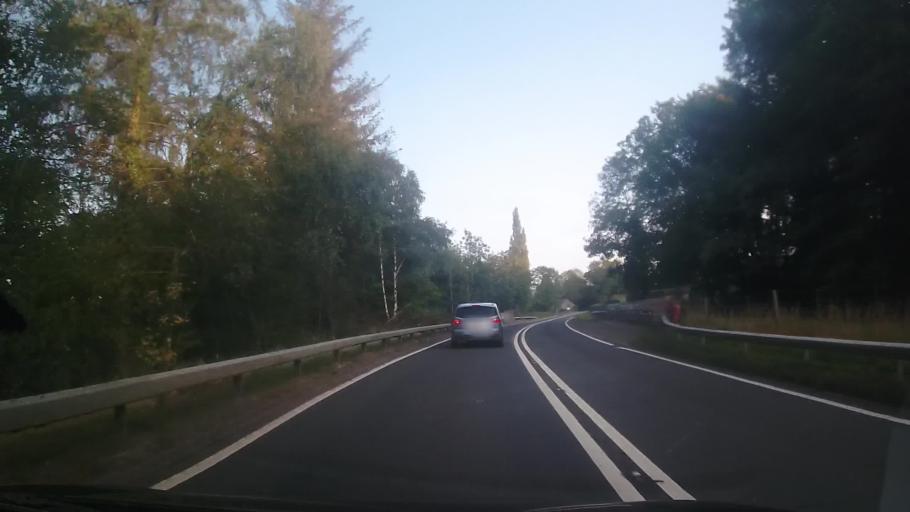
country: GB
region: Wales
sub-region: Sir Powys
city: Mochdre
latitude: 52.5154
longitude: -3.3756
